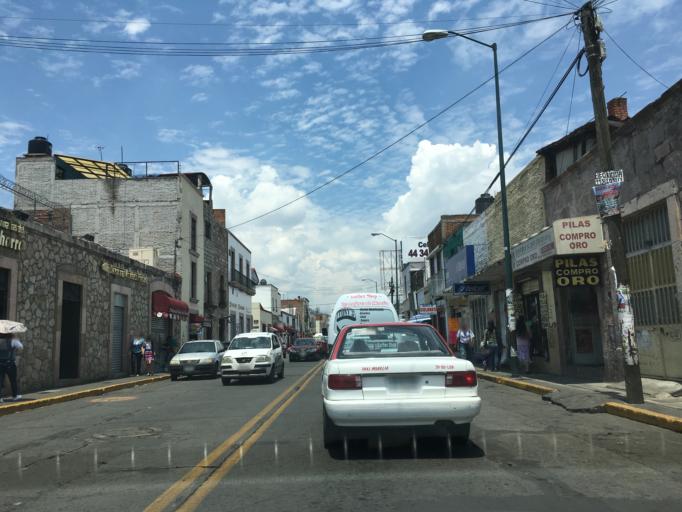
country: MX
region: Michoacan
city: Morelia
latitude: 19.6961
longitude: -101.1939
